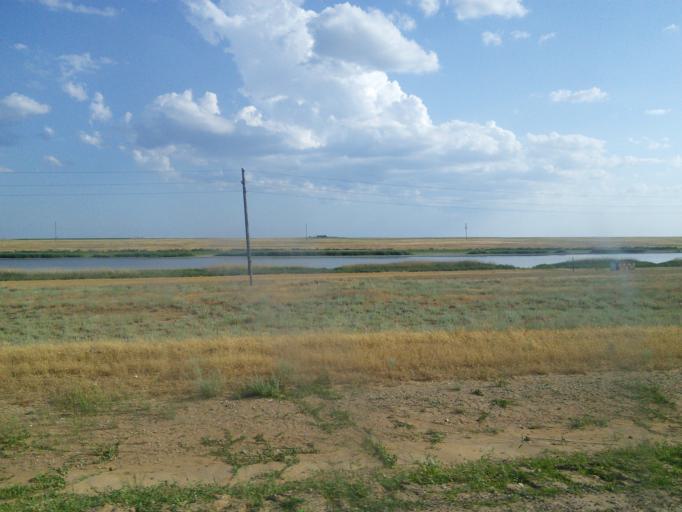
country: RU
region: Astrakhan
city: Ikryanoye
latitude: 46.2518
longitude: 47.6051
